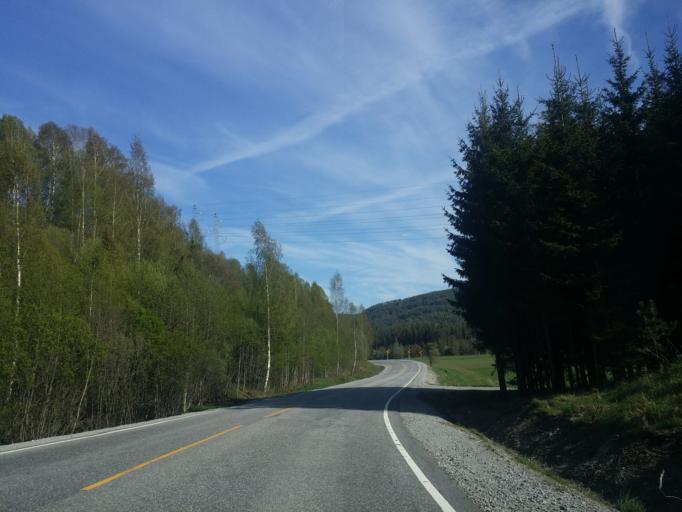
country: NO
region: Telemark
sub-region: Hjartdal
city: Sauland
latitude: 59.6228
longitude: 8.9096
